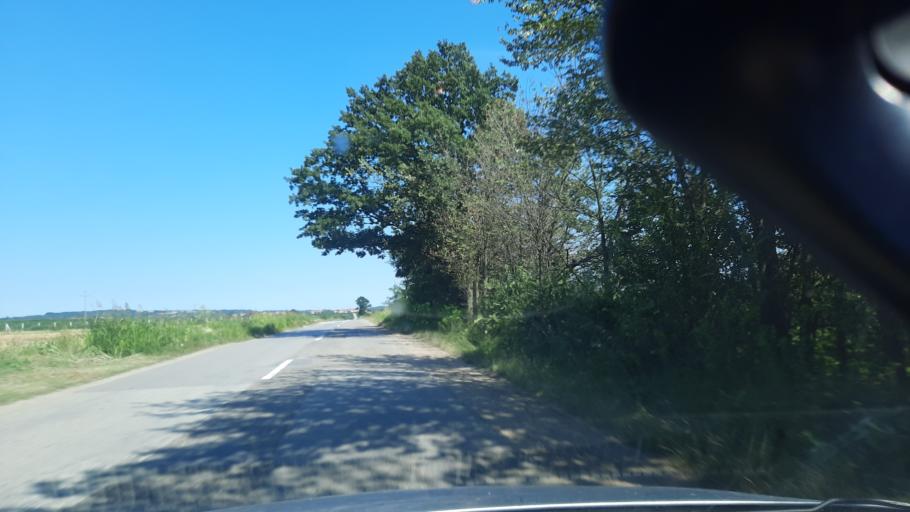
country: RS
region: Central Serbia
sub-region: Branicevski Okrug
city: Malo Crnice
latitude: 44.5778
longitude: 21.3340
